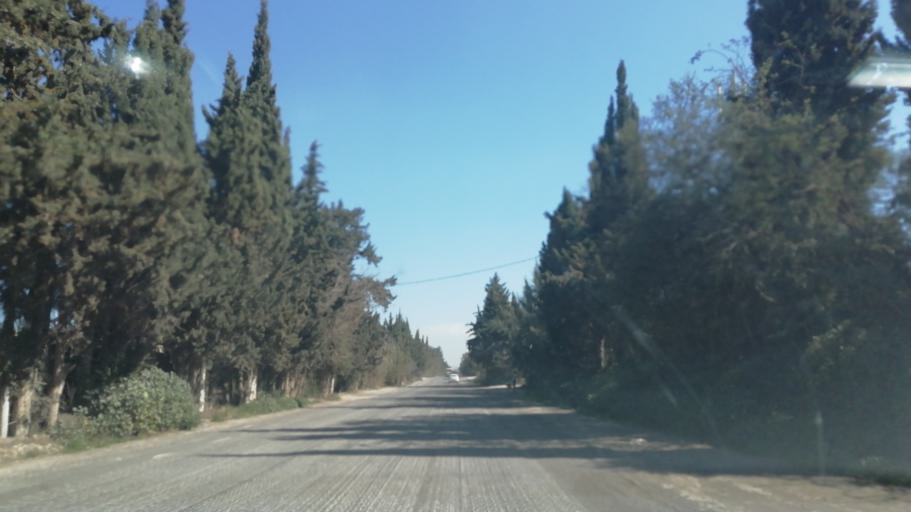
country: DZ
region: Mascara
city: Mascara
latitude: 35.5818
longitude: 0.0263
